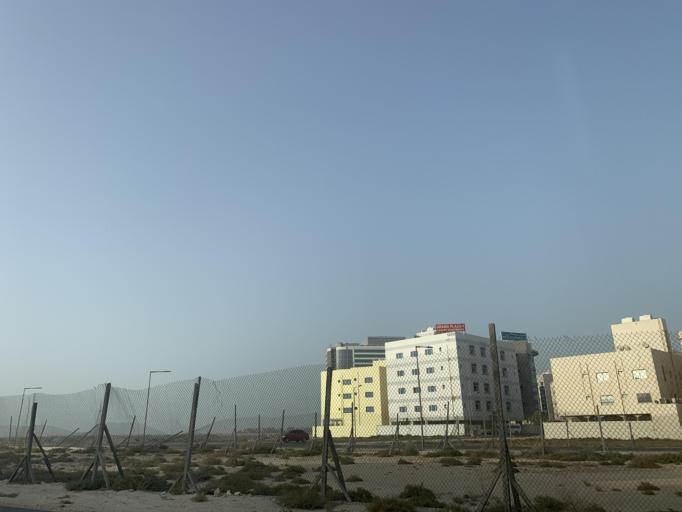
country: BH
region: Manama
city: Jidd Hafs
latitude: 26.2401
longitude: 50.5281
